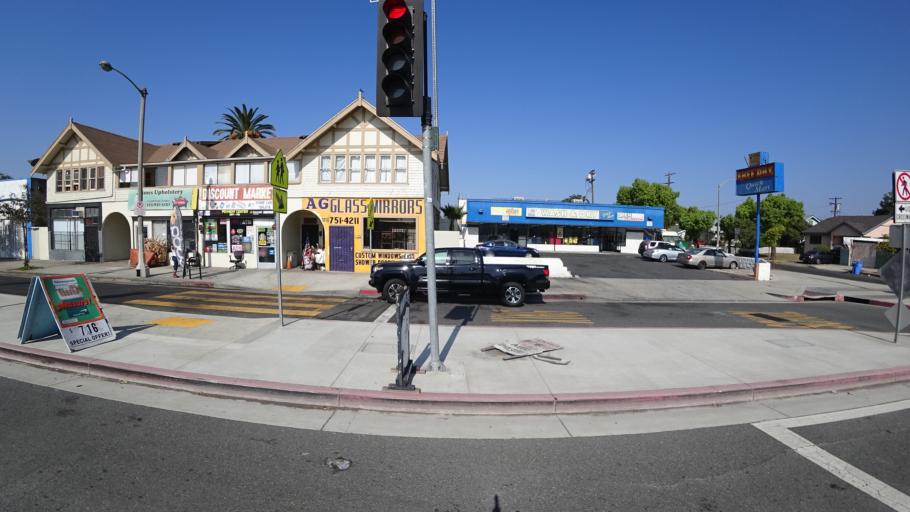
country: US
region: California
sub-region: Los Angeles County
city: Westmont
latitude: 33.9708
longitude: -118.2918
